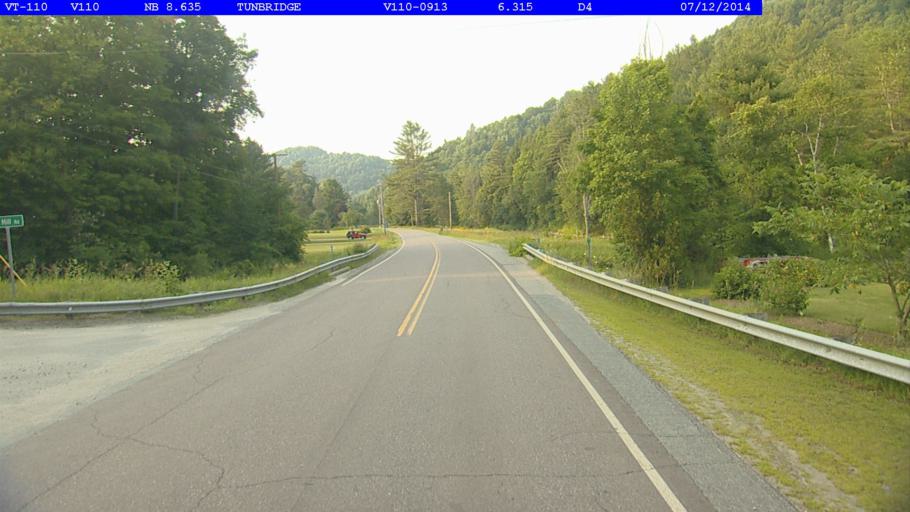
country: US
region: Vermont
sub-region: Orange County
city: Chelsea
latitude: 43.9304
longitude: -72.4664
